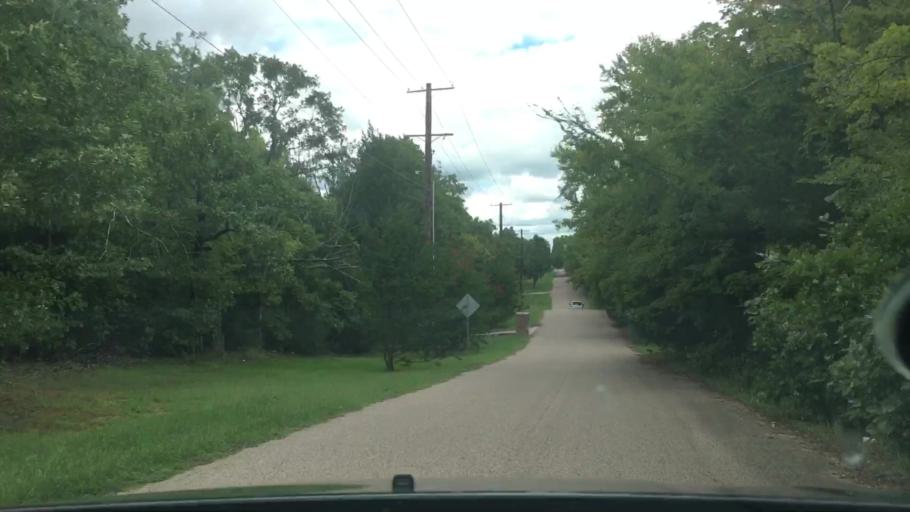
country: US
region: Oklahoma
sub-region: Pontotoc County
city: Ada
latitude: 34.7530
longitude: -96.6524
